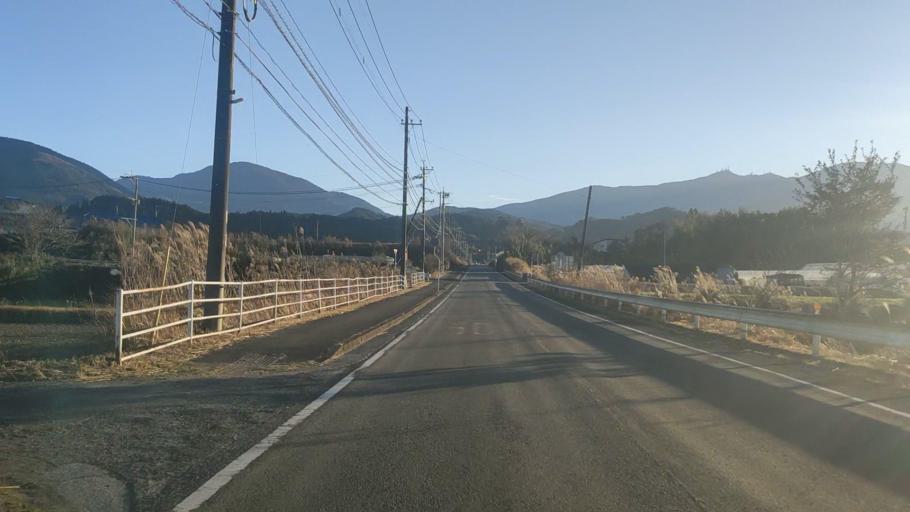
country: JP
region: Miyazaki
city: Miyazaki-shi
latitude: 31.8273
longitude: 131.2987
